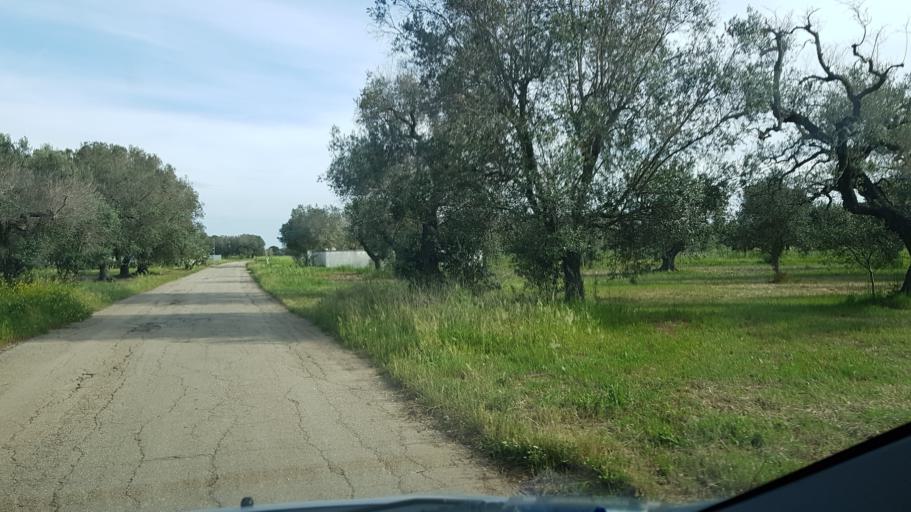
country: IT
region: Apulia
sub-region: Provincia di Brindisi
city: Tuturano
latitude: 40.5229
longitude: 17.9700
